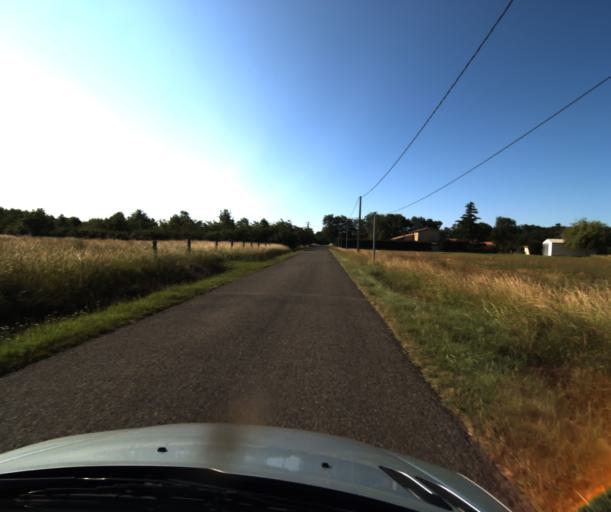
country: FR
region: Midi-Pyrenees
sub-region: Departement du Tarn-et-Garonne
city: Saint-Porquier
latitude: 44.0551
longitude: 1.2104
